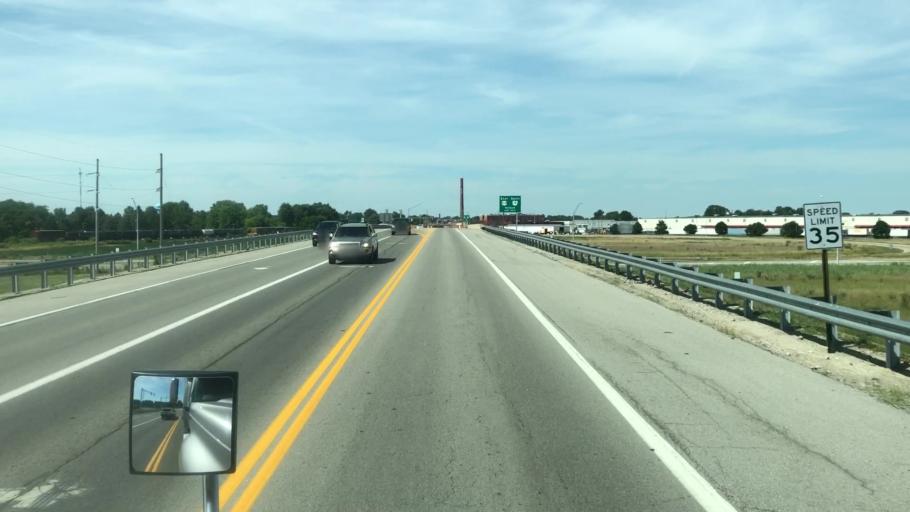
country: US
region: Ohio
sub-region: Sandusky County
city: Fremont
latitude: 41.3638
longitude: -83.0843
